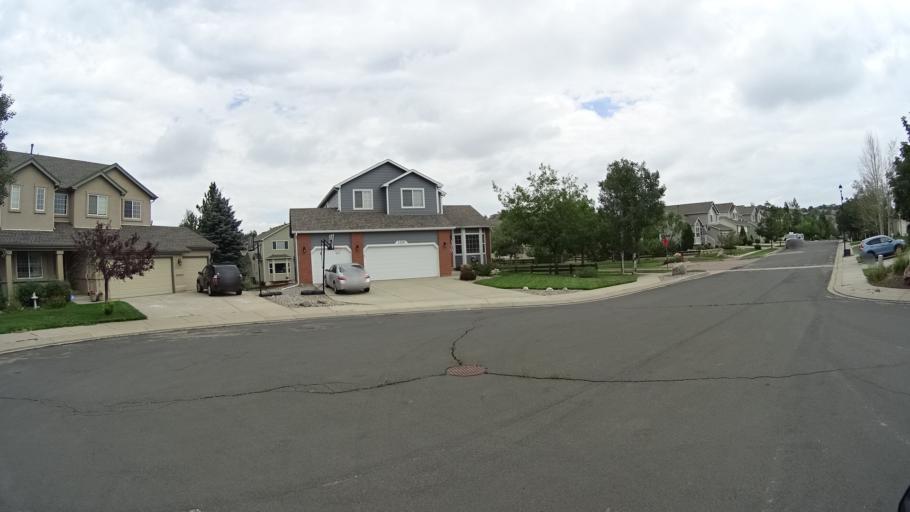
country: US
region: Colorado
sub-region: El Paso County
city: Gleneagle
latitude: 39.0065
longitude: -104.8022
